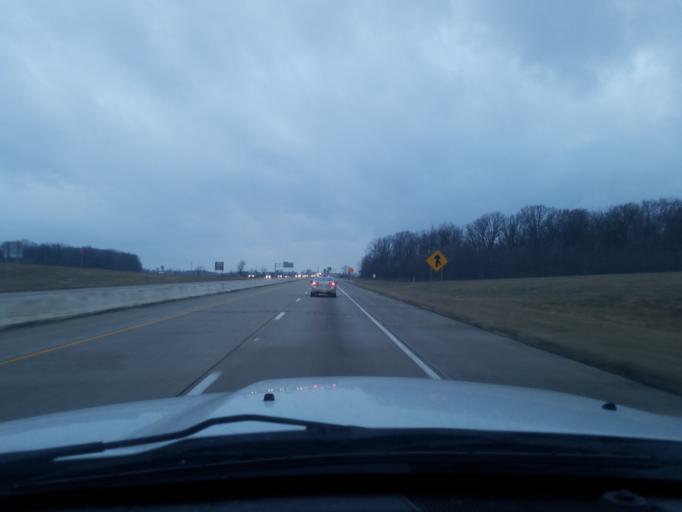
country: US
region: Indiana
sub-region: Huntington County
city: Roanoke
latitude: 40.9544
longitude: -85.2583
